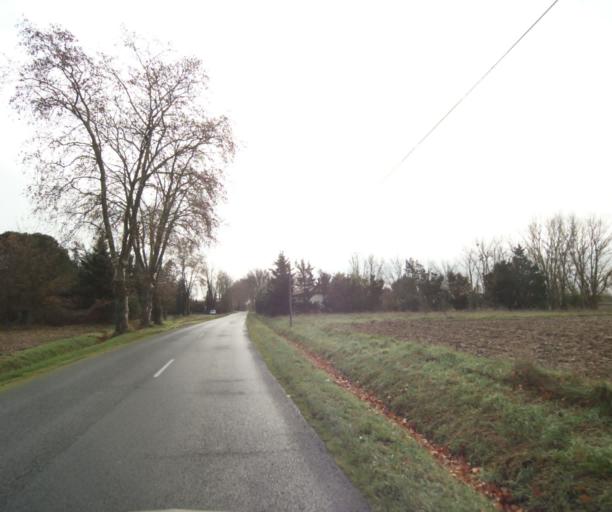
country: FR
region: Midi-Pyrenees
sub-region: Departement de la Haute-Garonne
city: Villemur-sur-Tarn
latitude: 43.8789
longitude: 1.4854
